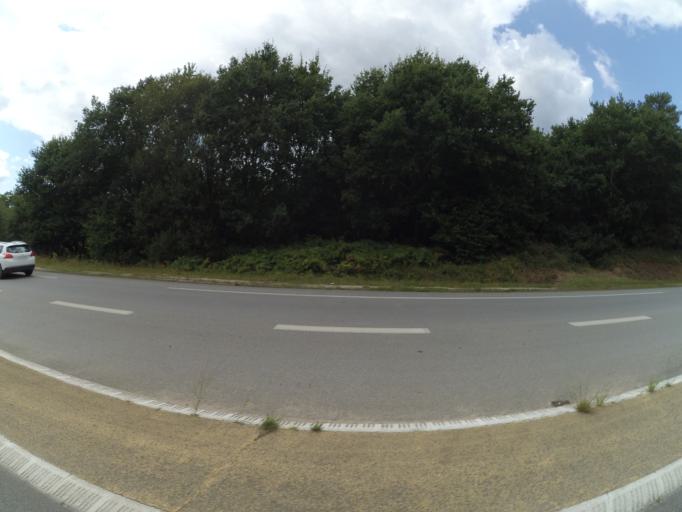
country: FR
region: Brittany
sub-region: Departement du Morbihan
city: Auray
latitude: 47.6899
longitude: -3.0084
